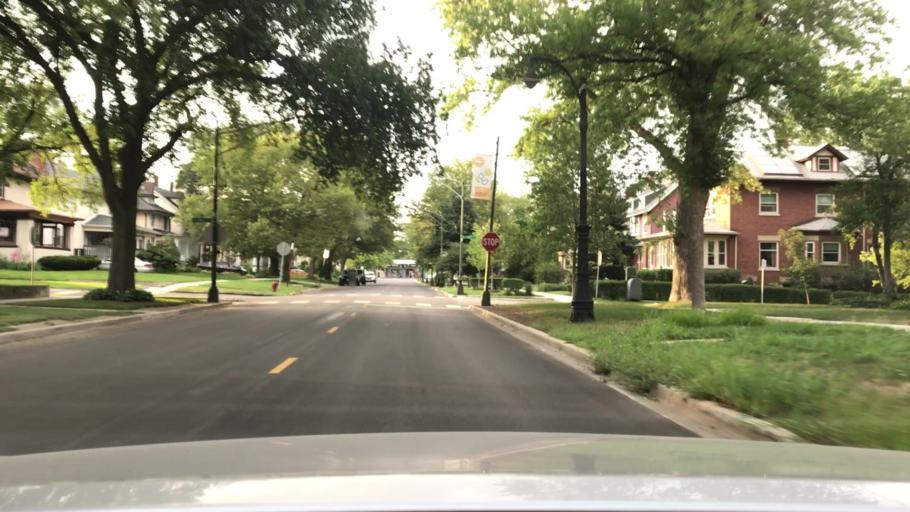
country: US
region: Illinois
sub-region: Cook County
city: Evergreen Park
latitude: 41.7189
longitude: -87.6691
